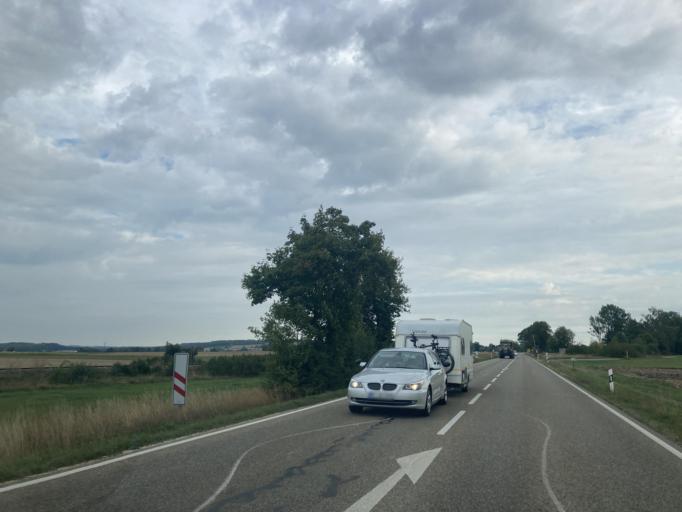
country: DE
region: Bavaria
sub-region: Swabia
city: Munningen
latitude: 48.9337
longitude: 10.5841
